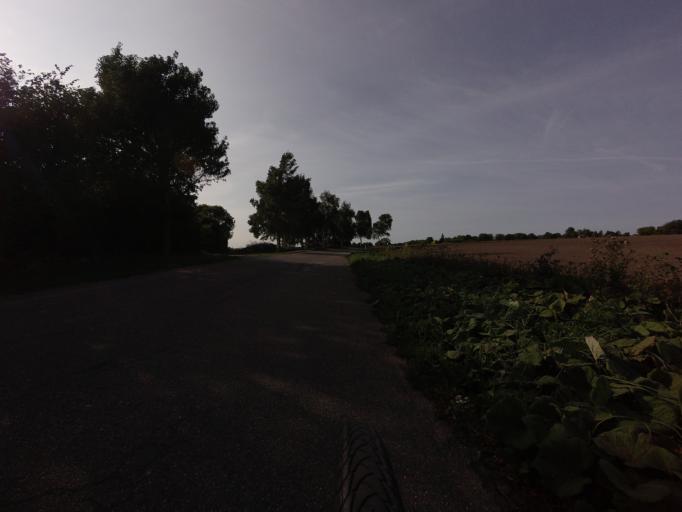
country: DK
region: Zealand
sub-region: Faxe Kommune
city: Fakse
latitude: 55.1924
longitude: 12.1092
